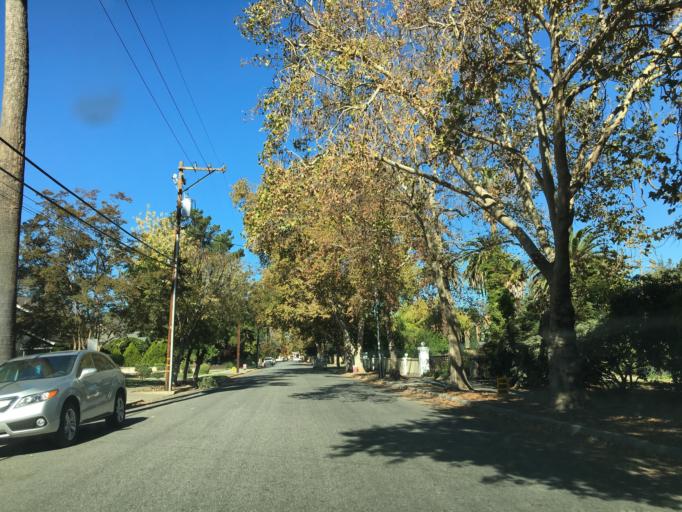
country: US
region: California
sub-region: Santa Clara County
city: Buena Vista
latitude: 37.2994
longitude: -121.8995
